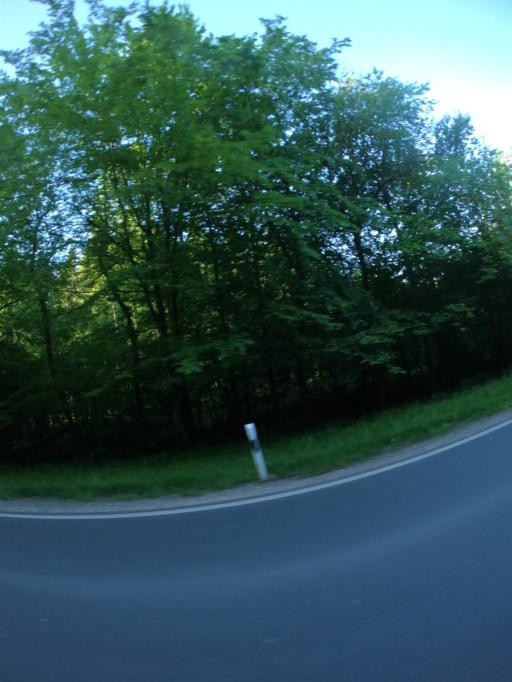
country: DE
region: Bavaria
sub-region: Upper Bavaria
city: Fraunberg
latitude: 48.3382
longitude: 12.0323
